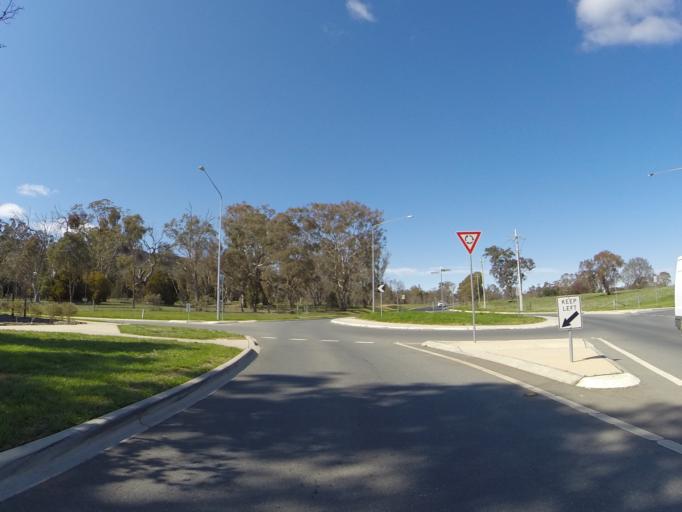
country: AU
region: Australian Capital Territory
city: Kaleen
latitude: -35.2282
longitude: 149.1667
